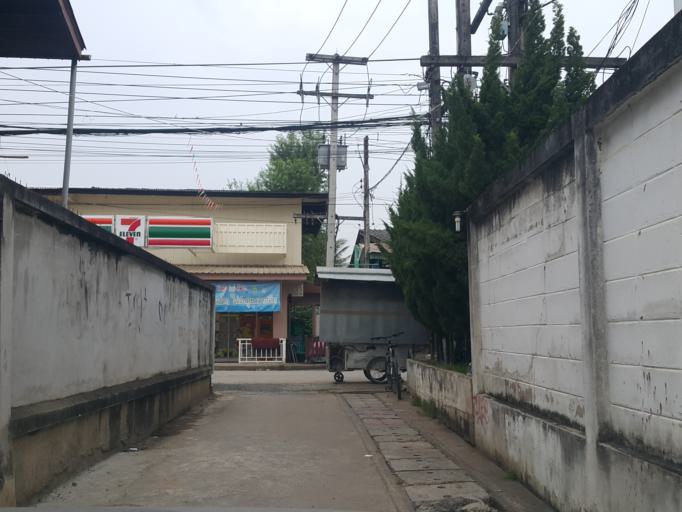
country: TH
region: Chiang Mai
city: Pai
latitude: 19.3593
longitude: 98.4414
